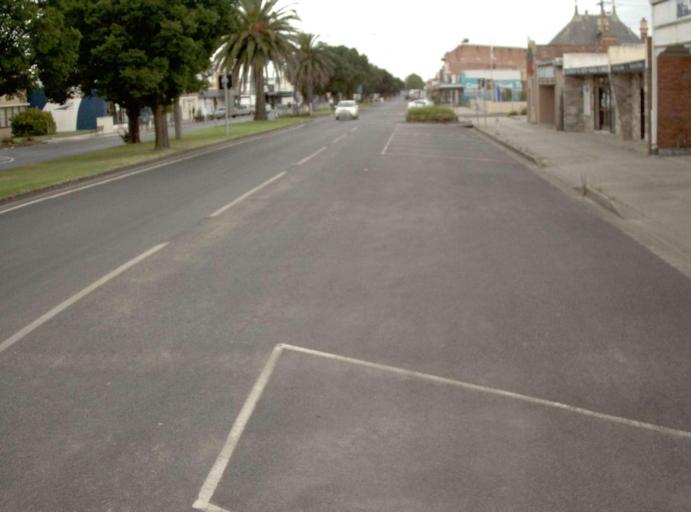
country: AU
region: Victoria
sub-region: Latrobe
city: Traralgon
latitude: -38.5605
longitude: 146.6765
